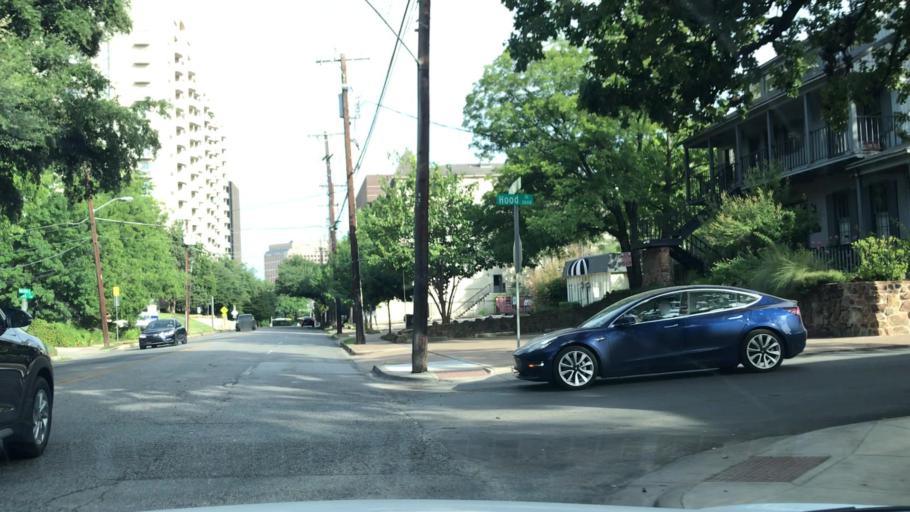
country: US
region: Texas
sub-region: Dallas County
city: Dallas
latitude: 32.8076
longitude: -96.8069
